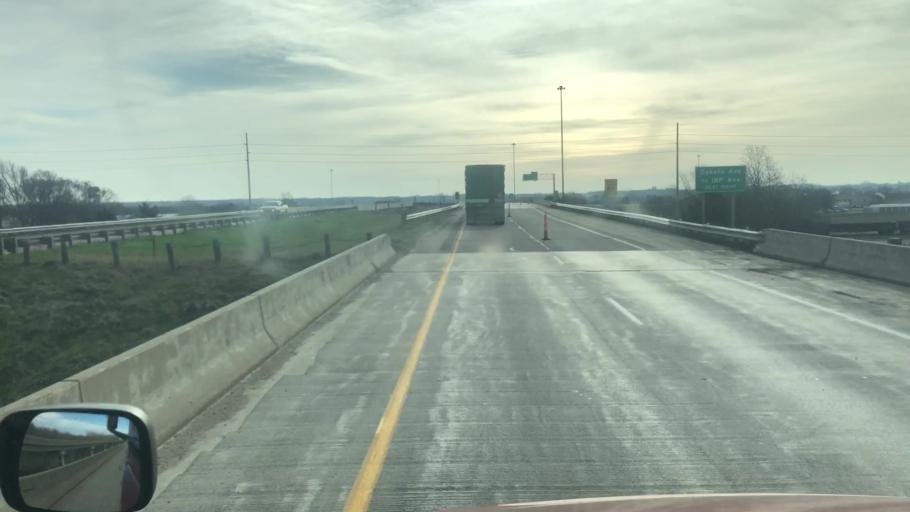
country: US
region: Nebraska
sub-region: Dakota County
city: South Sioux City
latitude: 42.4491
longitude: -96.4215
